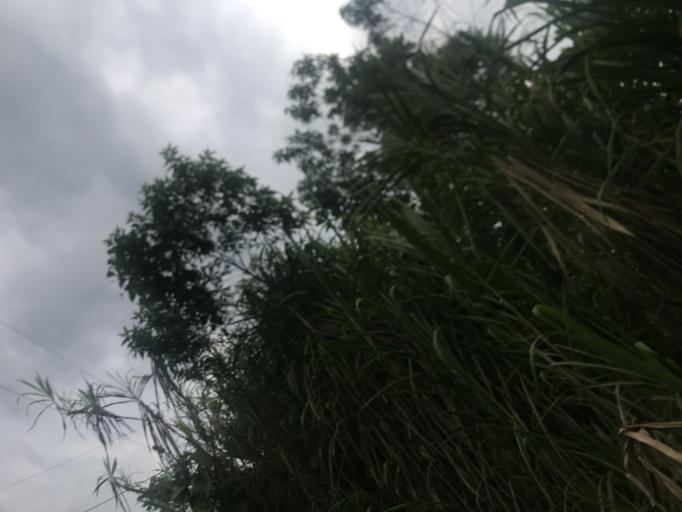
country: EC
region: Napo
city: Tena
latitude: -1.0245
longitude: -77.7417
